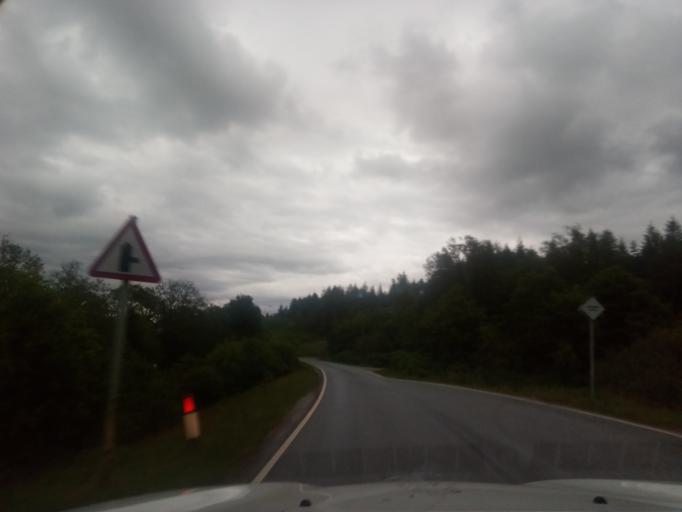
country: GB
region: Scotland
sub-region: Highland
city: Fort William
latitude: 56.8553
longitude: -5.3446
